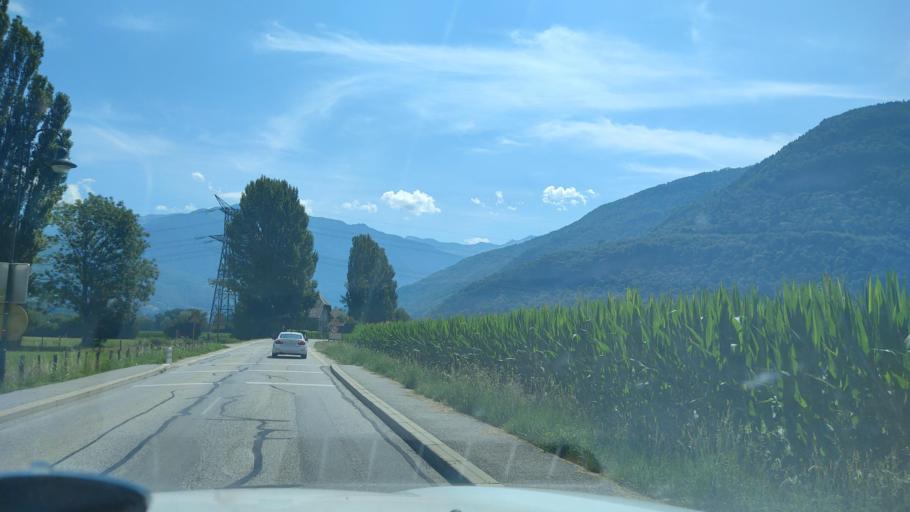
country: FR
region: Rhone-Alpes
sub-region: Departement de la Savoie
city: Aiton
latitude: 45.5521
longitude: 6.2242
